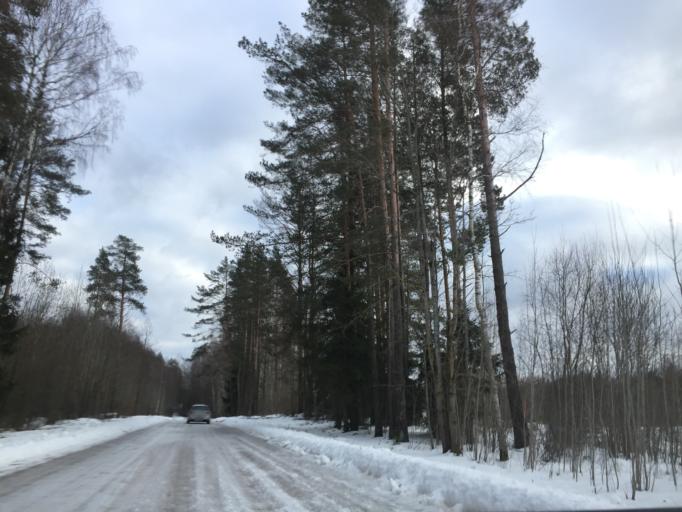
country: LV
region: Lielvarde
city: Lielvarde
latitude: 56.5803
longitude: 24.7720
